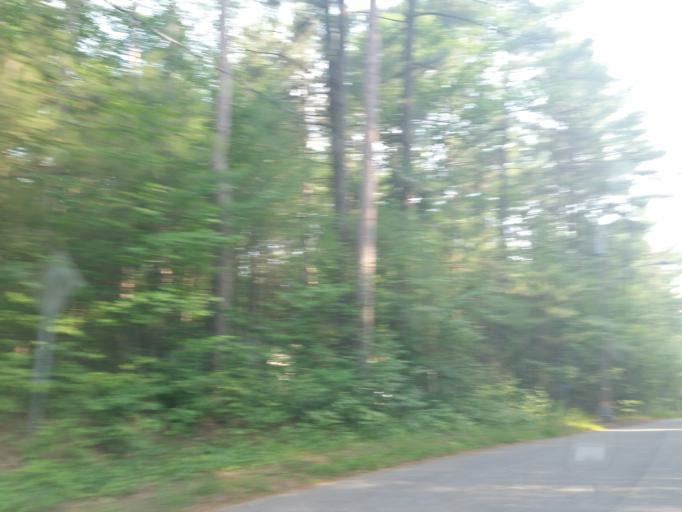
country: CA
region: Quebec
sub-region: Outaouais
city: Shawville
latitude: 45.5184
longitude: -76.4154
